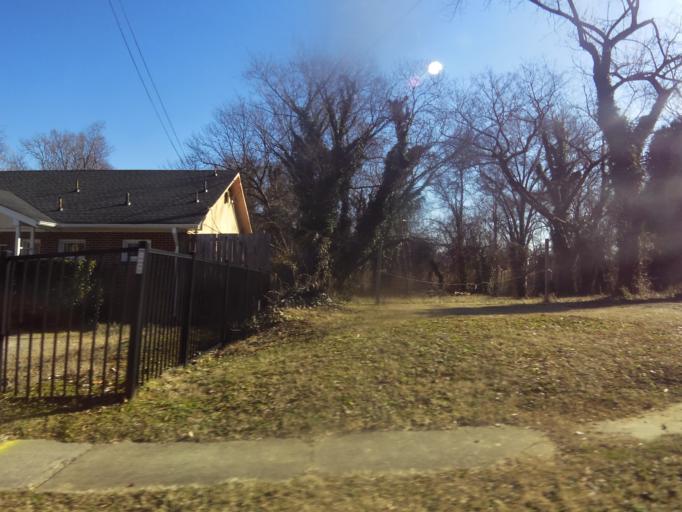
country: US
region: Virginia
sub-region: City of Richmond
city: Richmond
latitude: 37.5596
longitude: -77.4302
